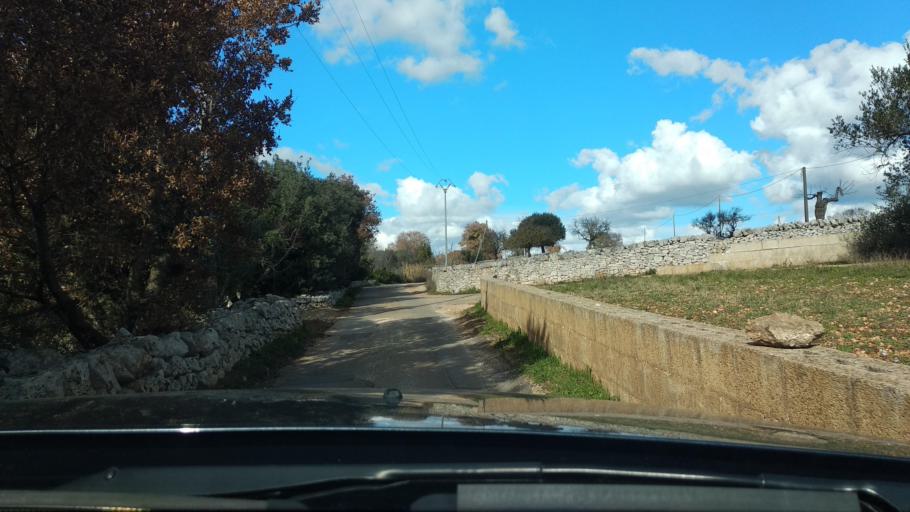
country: IT
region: Apulia
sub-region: Provincia di Brindisi
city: Casalini
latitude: 40.7077
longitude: 17.4534
